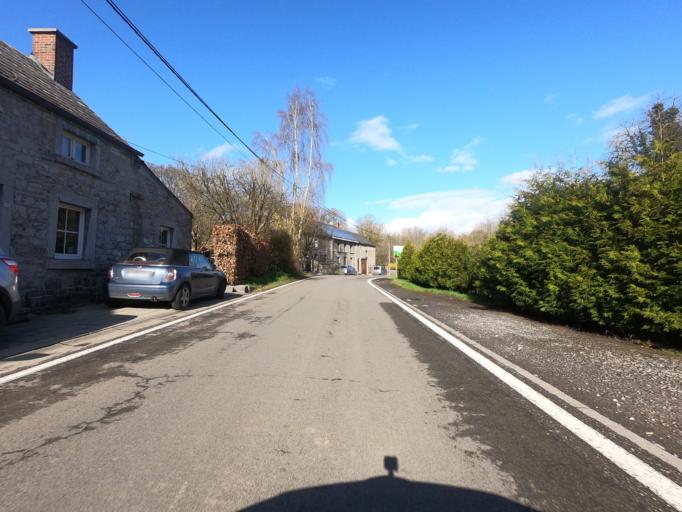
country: BE
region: Wallonia
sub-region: Province de Namur
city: Mettet
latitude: 50.3006
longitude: 4.7252
